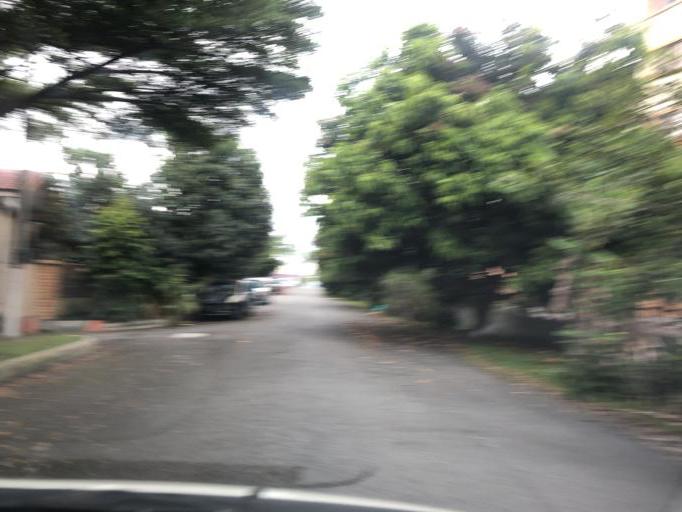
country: MY
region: Putrajaya
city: Putrajaya
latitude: 2.9252
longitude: 101.7605
